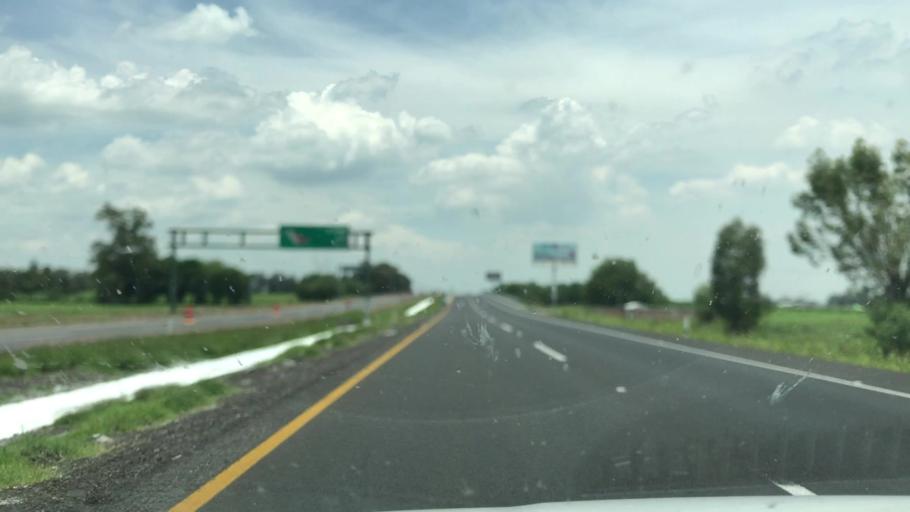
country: MX
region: Guanajuato
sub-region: Irapuato
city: Cuarta Brigada
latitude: 20.6514
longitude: -101.2843
